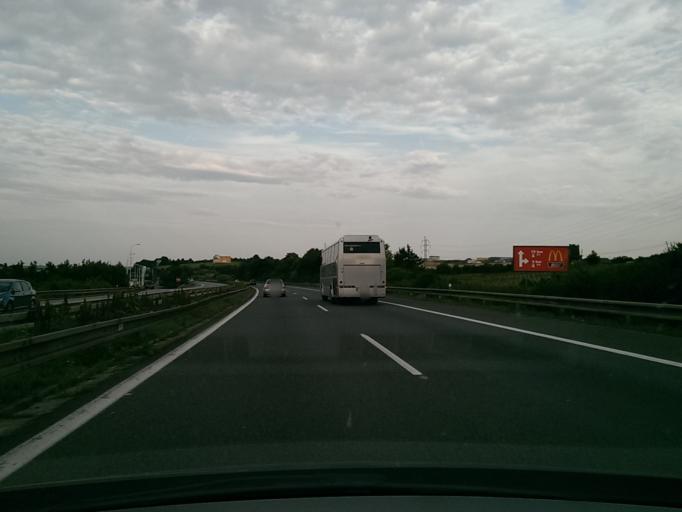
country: CZ
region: South Moravian
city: Moravany
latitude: 49.1609
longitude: 16.5669
